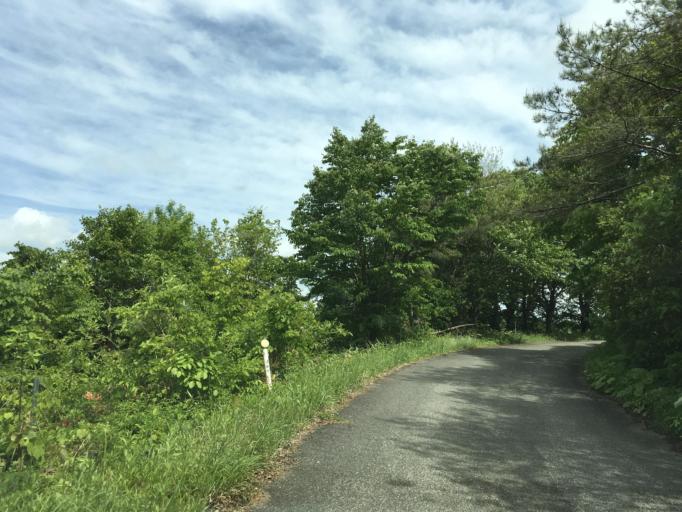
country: JP
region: Iwate
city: Mizusawa
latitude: 39.1343
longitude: 141.3151
